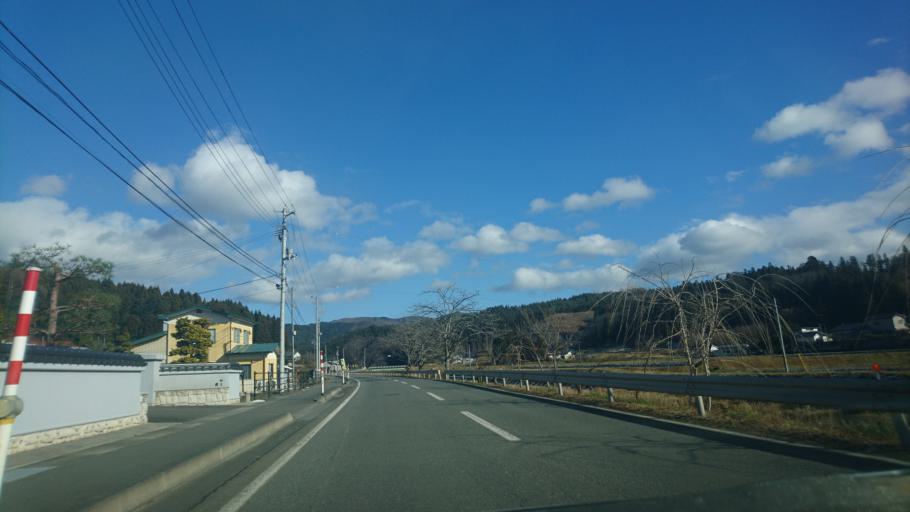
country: JP
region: Iwate
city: Mizusawa
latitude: 39.0581
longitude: 141.3677
